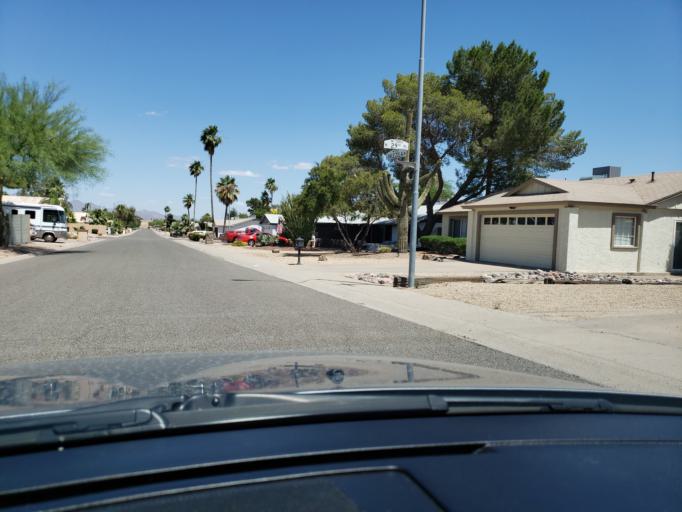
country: US
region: Arizona
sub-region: Maricopa County
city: Paradise Valley
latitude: 33.6079
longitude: -112.0186
